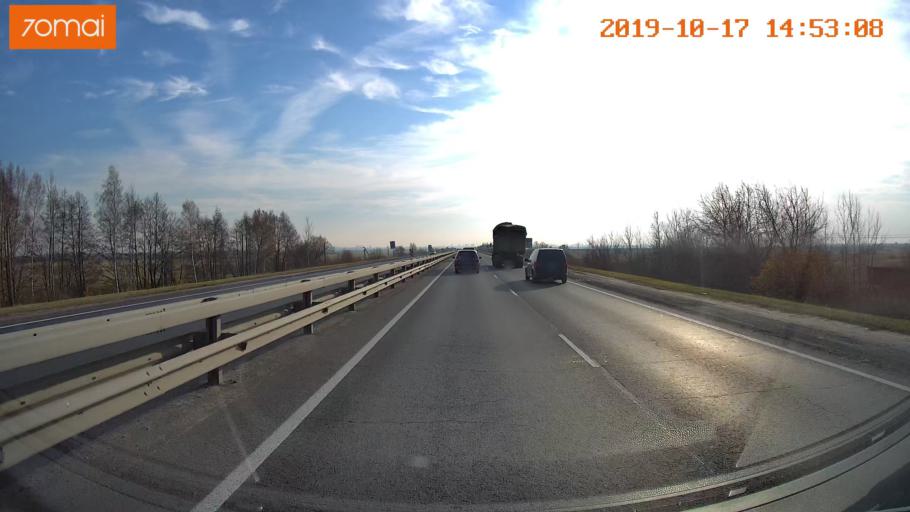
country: RU
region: Rjazan
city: Polyany
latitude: 54.6978
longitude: 39.8406
